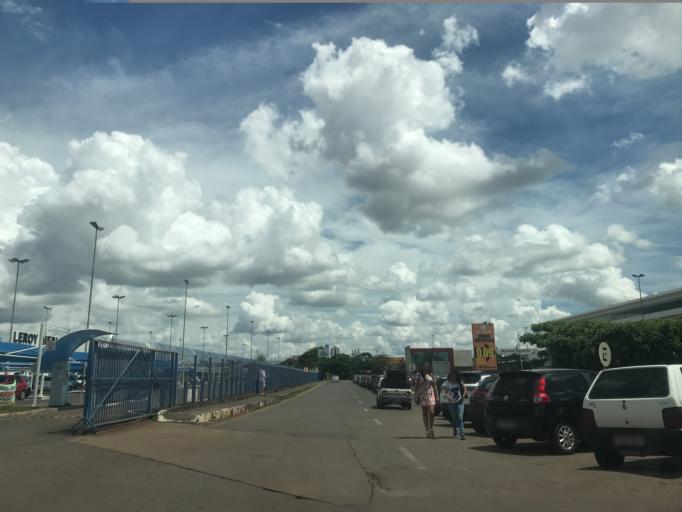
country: BR
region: Federal District
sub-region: Brasilia
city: Brasilia
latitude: -15.8429
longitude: -48.0437
